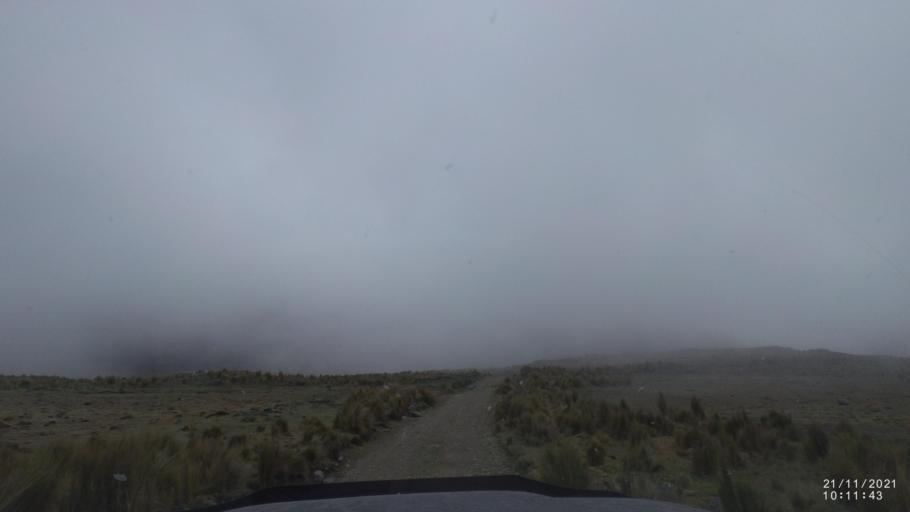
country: BO
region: Cochabamba
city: Cochabamba
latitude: -16.9929
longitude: -66.2695
